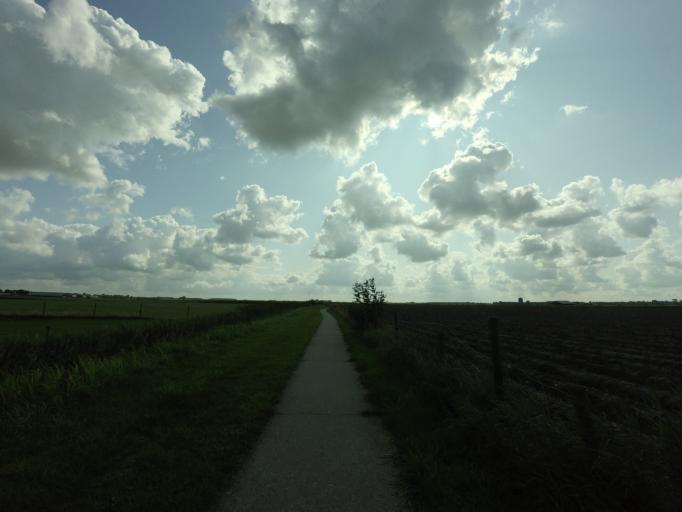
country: NL
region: Friesland
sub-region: Gemeente Het Bildt
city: Sint Jacobiparochie
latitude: 53.2692
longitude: 5.6068
